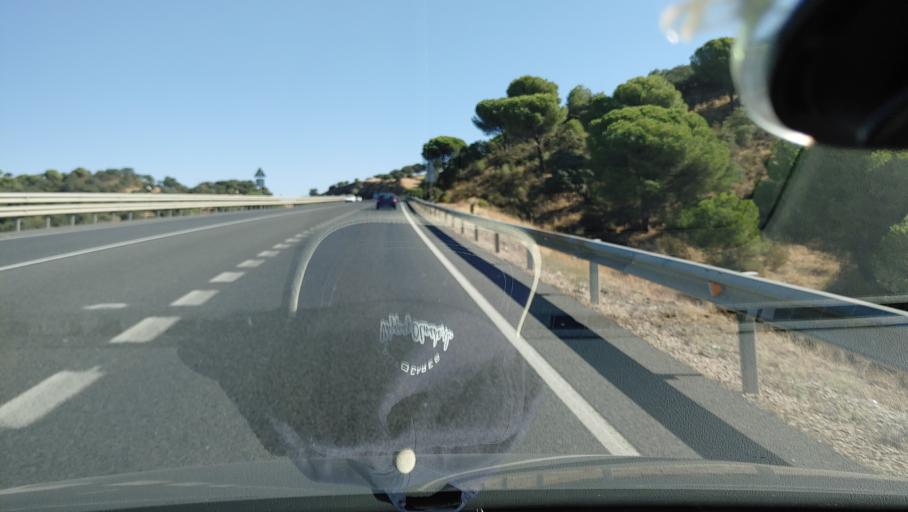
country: ES
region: Andalusia
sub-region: Province of Cordoba
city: Cordoba
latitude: 37.9851
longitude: -4.7872
